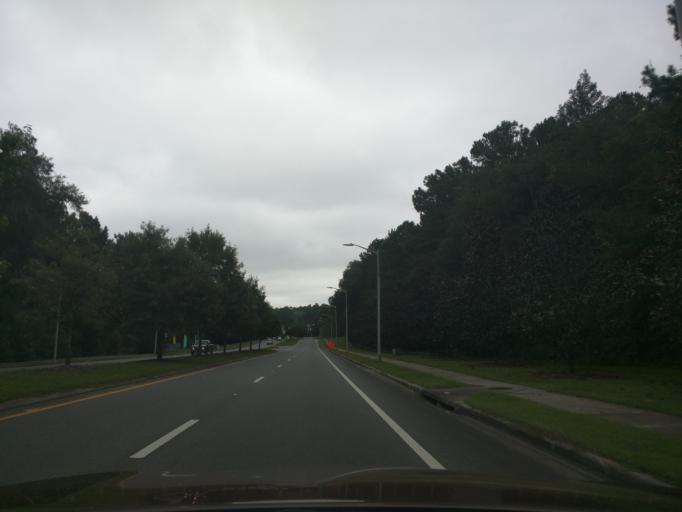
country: US
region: Florida
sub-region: Leon County
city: Tallahassee
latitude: 30.4305
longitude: -84.2023
